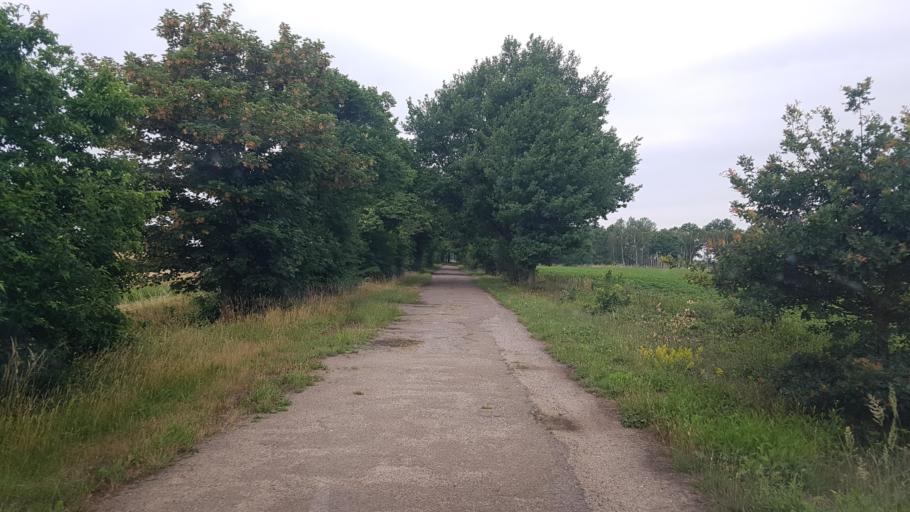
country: DE
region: Saxony-Anhalt
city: Annaburg
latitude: 51.7587
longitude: 13.0076
